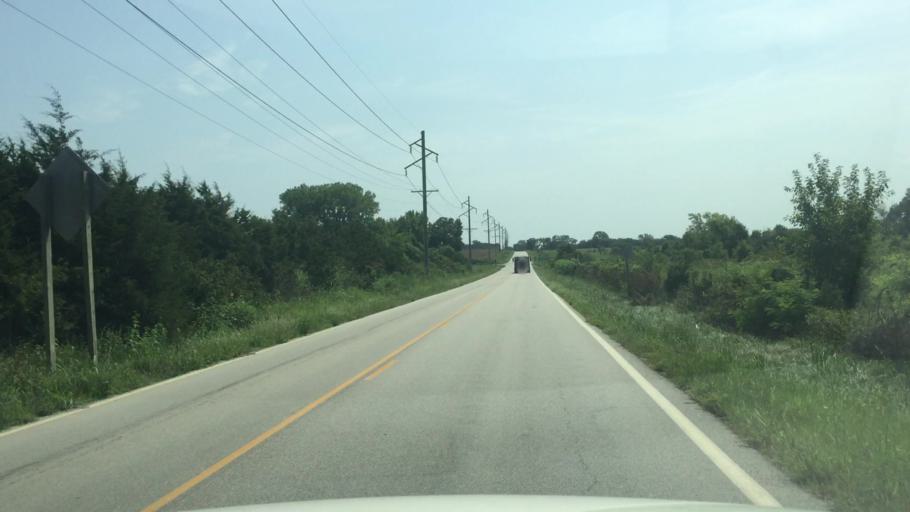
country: US
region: Kansas
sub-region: Montgomery County
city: Cherryvale
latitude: 37.2089
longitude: -95.5796
